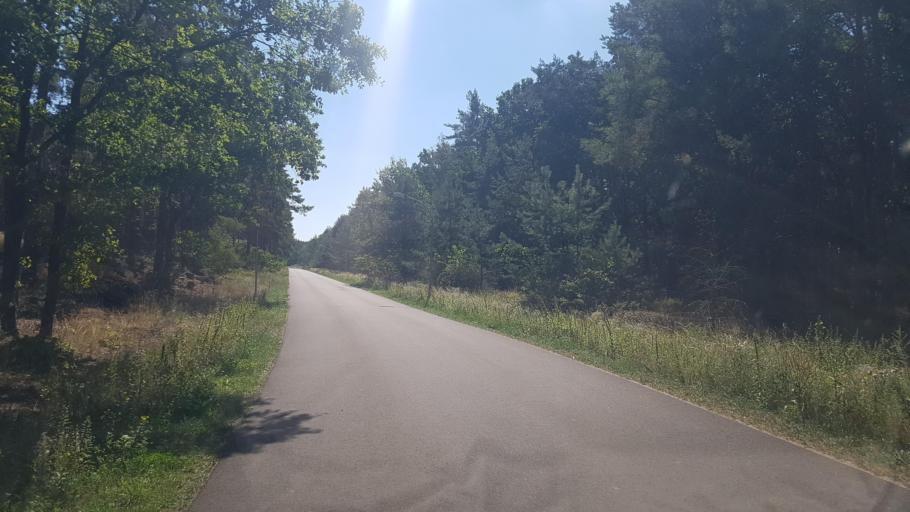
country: DE
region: Brandenburg
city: Golzow
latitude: 52.2922
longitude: 12.5883
